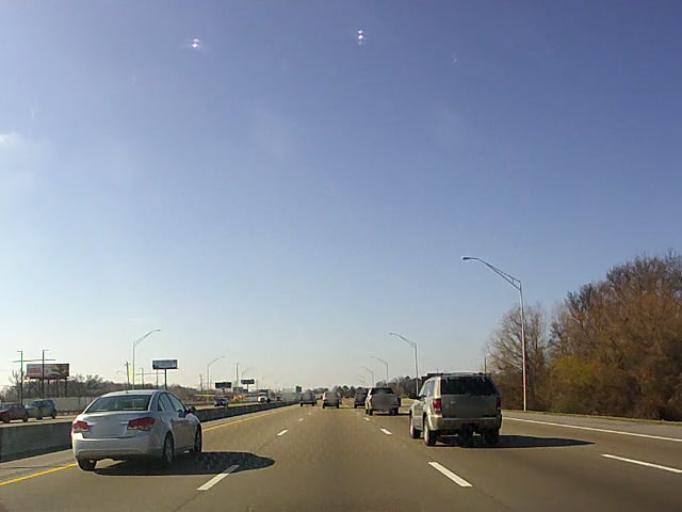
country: US
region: Tennessee
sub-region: Shelby County
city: New South Memphis
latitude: 35.0768
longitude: -89.9739
